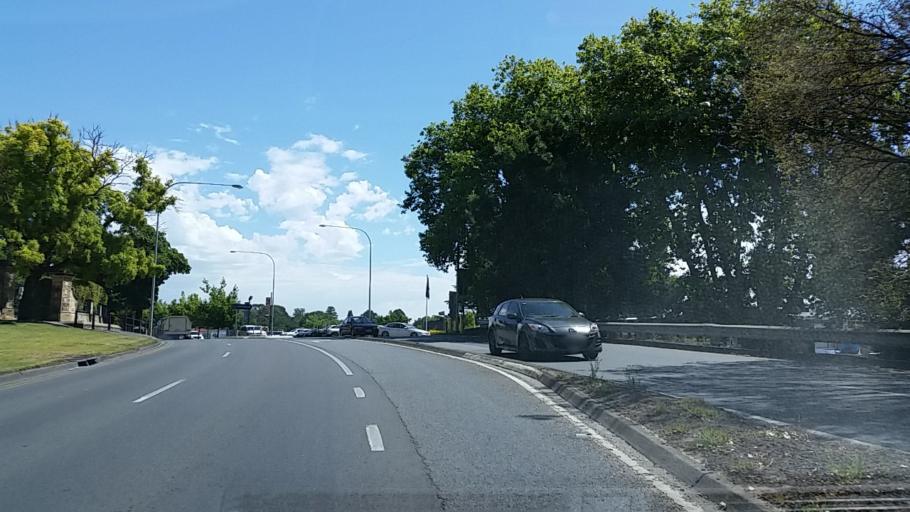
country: AU
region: South Australia
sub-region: Mount Barker
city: Mount Barker
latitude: -35.0684
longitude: 138.8572
